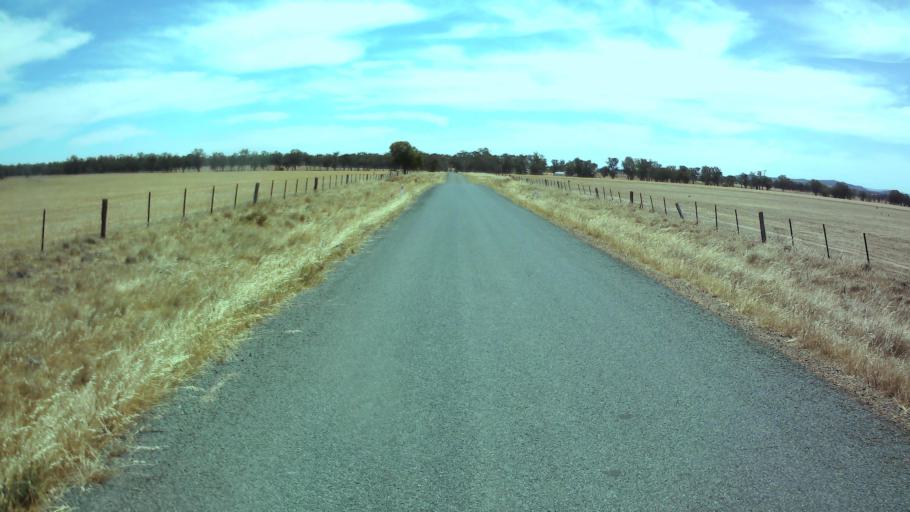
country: AU
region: New South Wales
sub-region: Weddin
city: Grenfell
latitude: -33.7470
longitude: 148.2075
